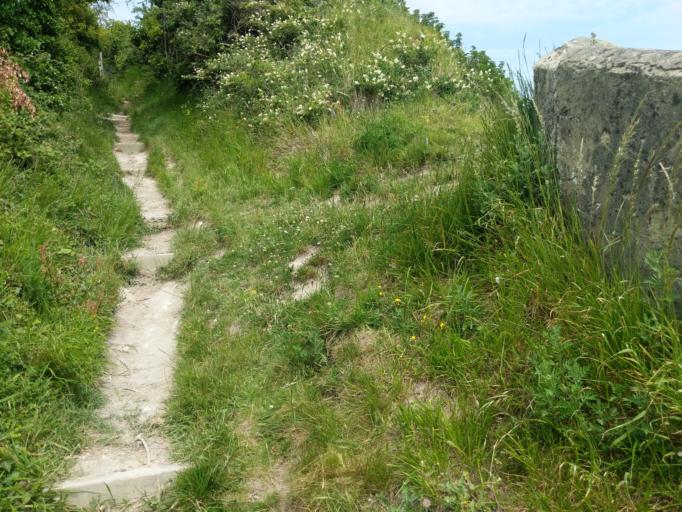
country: GB
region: England
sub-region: Kent
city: Folkestone
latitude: 51.0924
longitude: 1.1989
